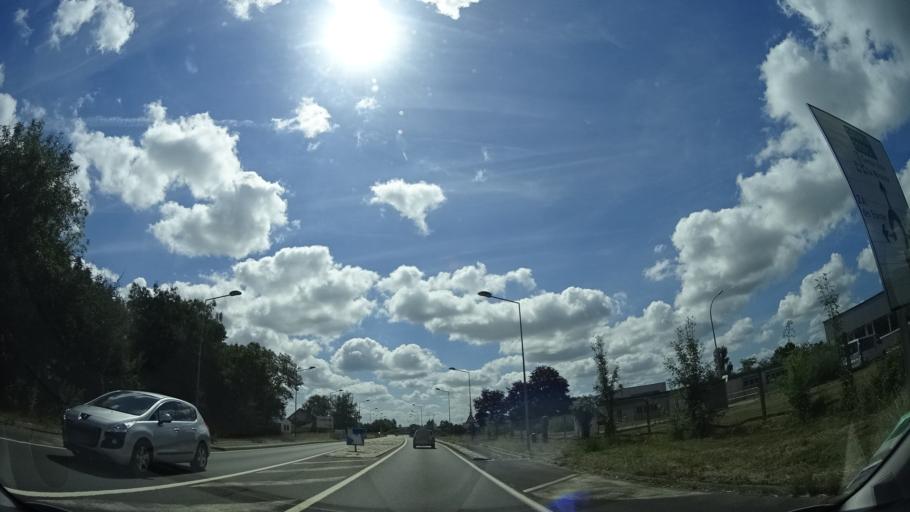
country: FR
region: Pays de la Loire
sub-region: Departement de la Sarthe
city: La Fleche
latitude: 47.7135
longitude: -0.1011
